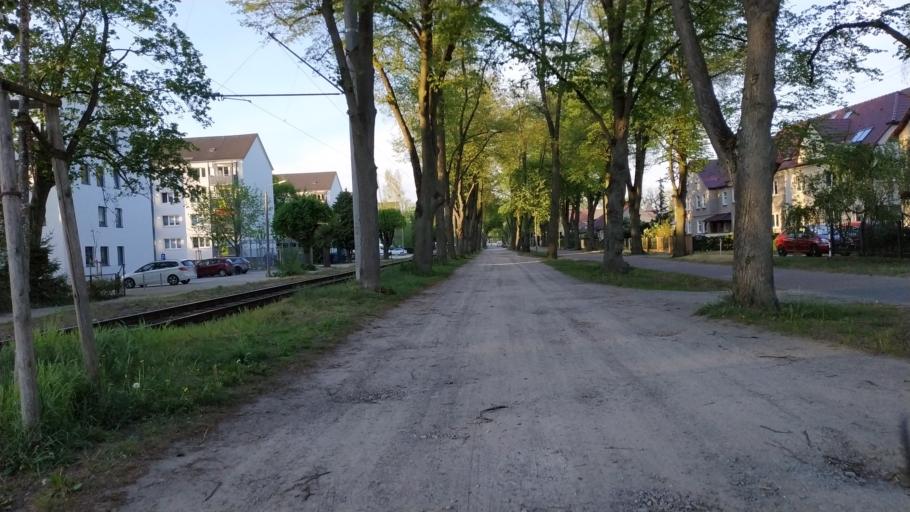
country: DE
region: Brandenburg
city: Petershagen
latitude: 52.5347
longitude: 13.8418
